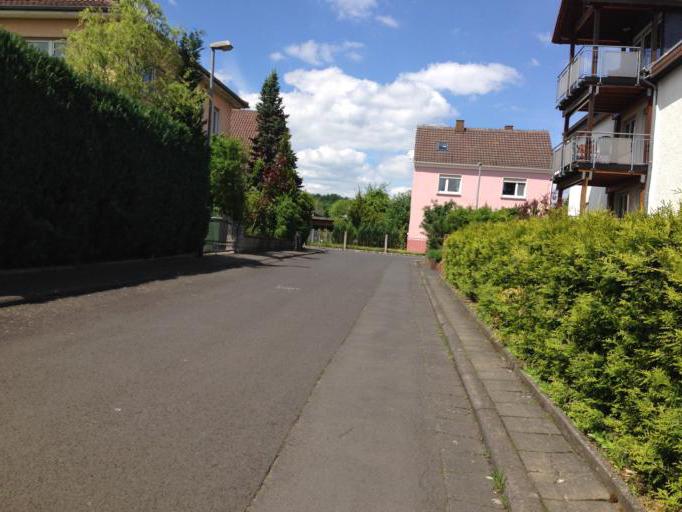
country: DE
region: Hesse
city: Lollar
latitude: 50.6621
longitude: 8.7095
